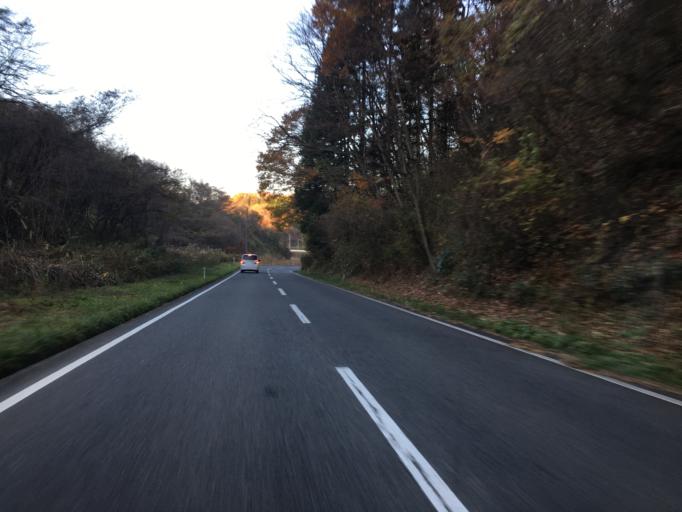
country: JP
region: Fukushima
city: Motomiya
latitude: 37.5249
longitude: 140.4602
